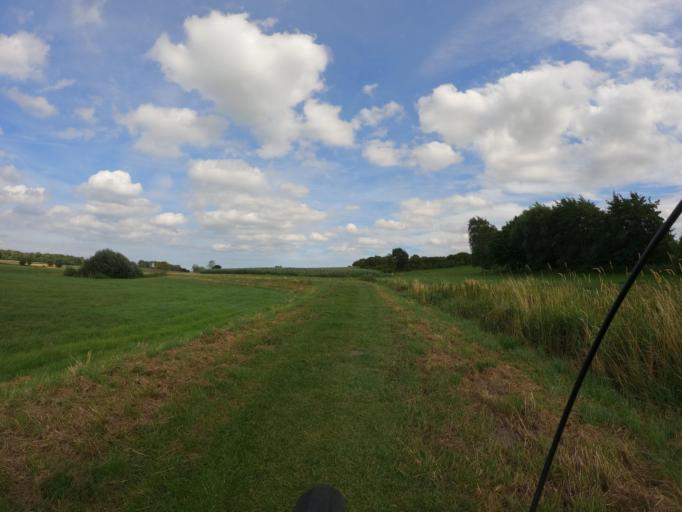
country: DE
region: Schleswig-Holstein
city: Niesgrau
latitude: 54.7549
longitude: 9.8176
